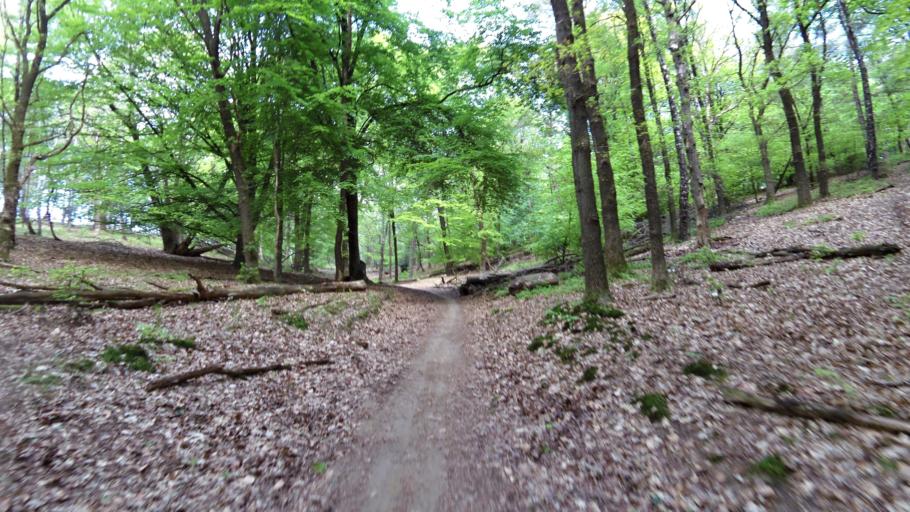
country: NL
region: Gelderland
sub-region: Gemeente Rheden
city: Rheden
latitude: 52.0224
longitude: 6.0356
